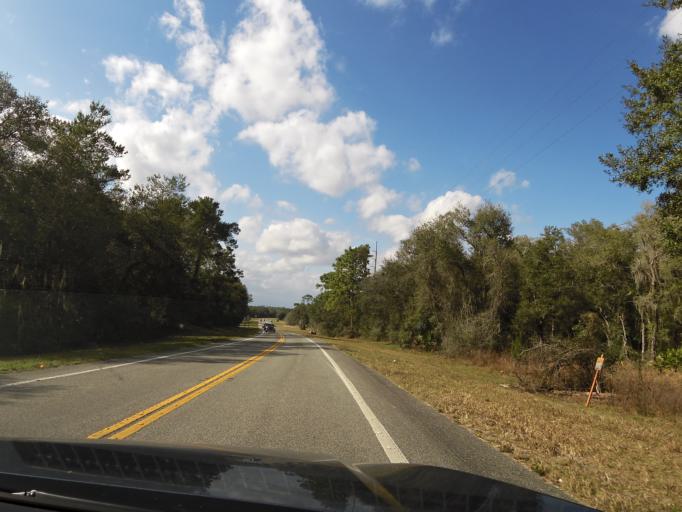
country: US
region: Florida
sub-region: Volusia County
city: De Leon Springs
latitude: 29.1378
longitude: -81.3551
